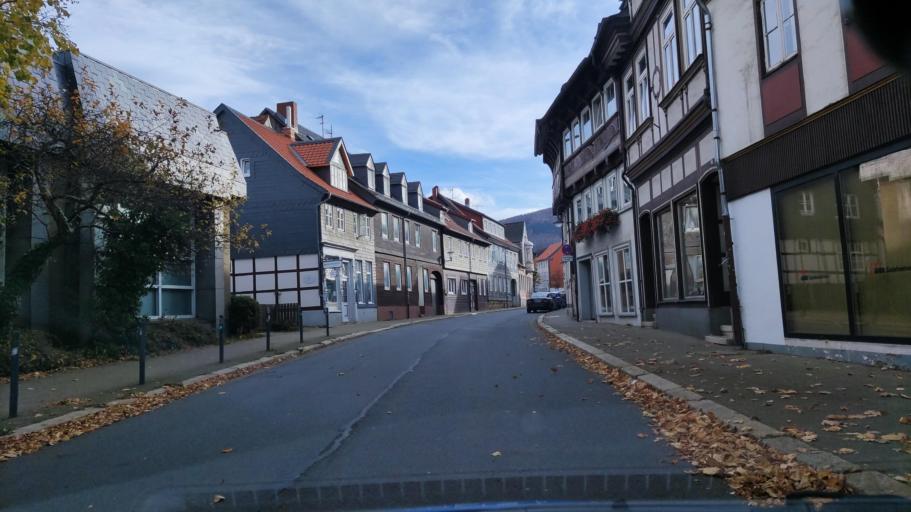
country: DE
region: Lower Saxony
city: Goslar
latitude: 51.9077
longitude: 10.4208
